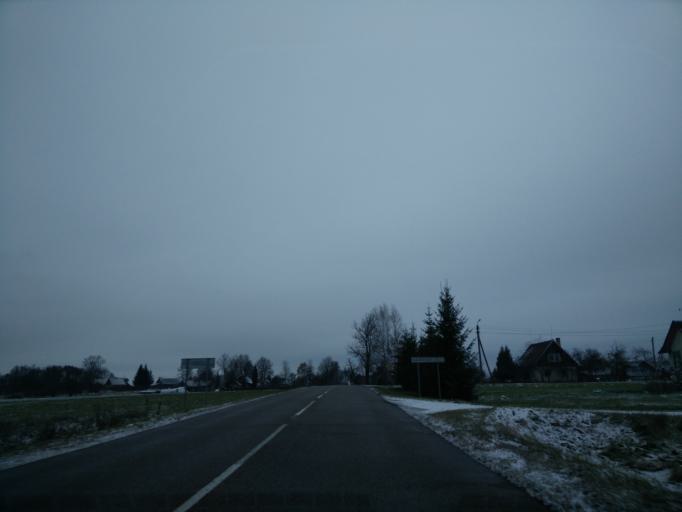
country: LT
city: Ariogala
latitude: 55.4196
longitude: 23.3457
